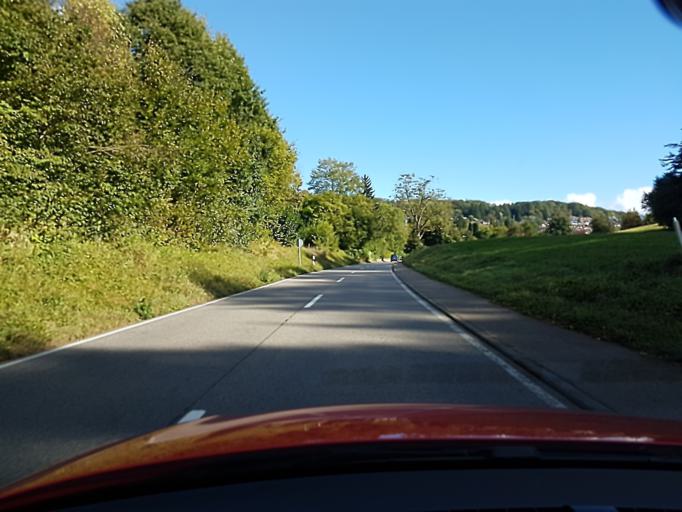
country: DE
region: Hesse
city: Neckarsteinach
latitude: 49.3951
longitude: 8.8369
